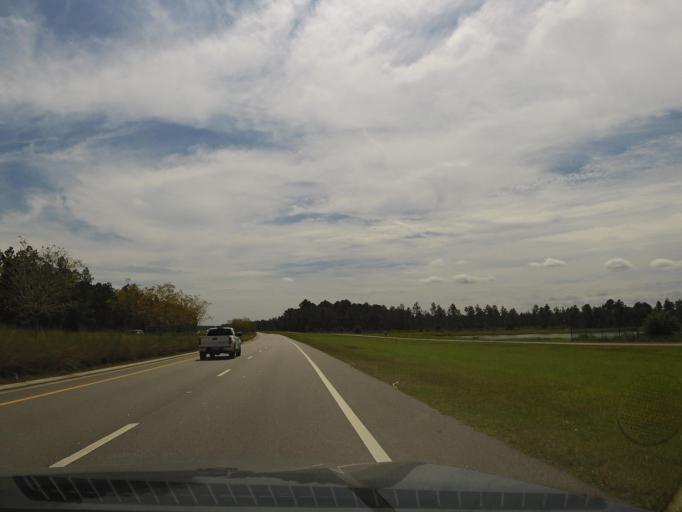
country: US
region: Florida
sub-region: Saint Johns County
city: Fruit Cove
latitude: 30.0266
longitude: -81.5230
